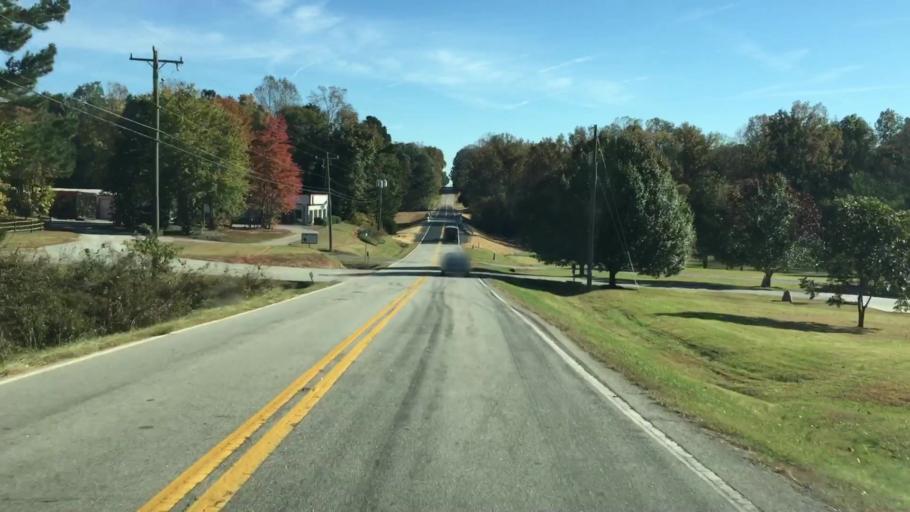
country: US
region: North Carolina
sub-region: Rowan County
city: China Grove
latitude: 35.6418
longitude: -80.6527
